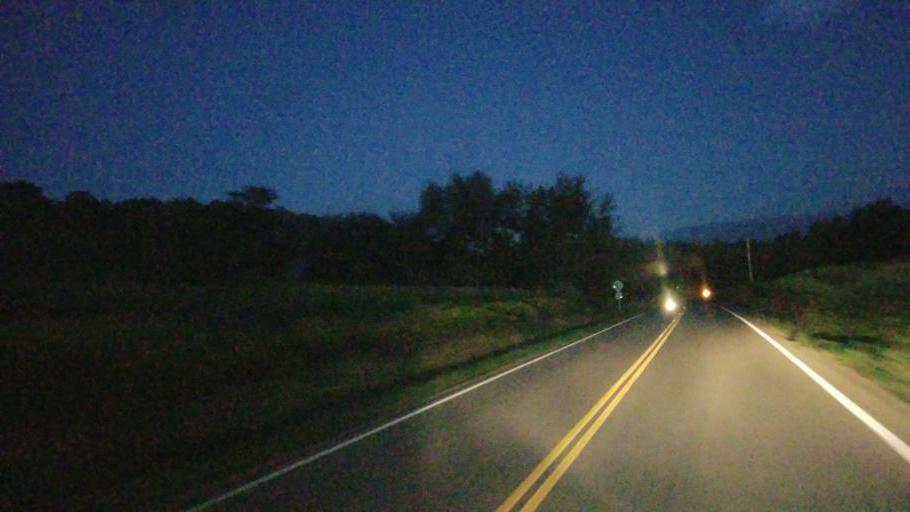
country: US
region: Ohio
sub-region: Ashland County
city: Ashland
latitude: 40.7914
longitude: -82.3821
